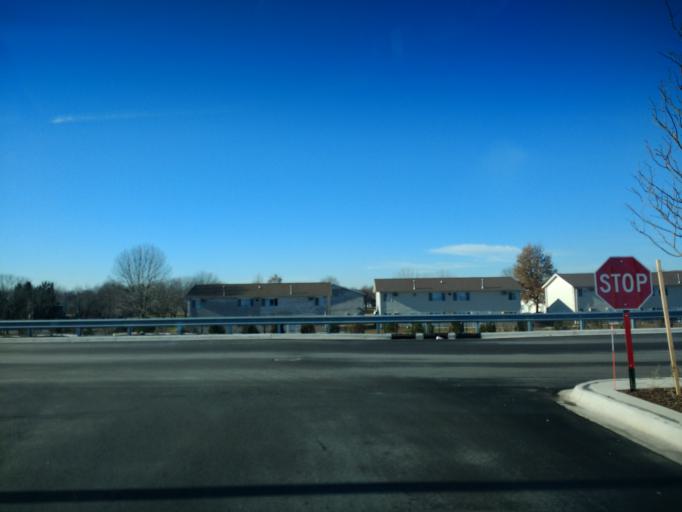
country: US
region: Iowa
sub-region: Scott County
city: Bettendorf
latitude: 41.5756
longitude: -90.5344
